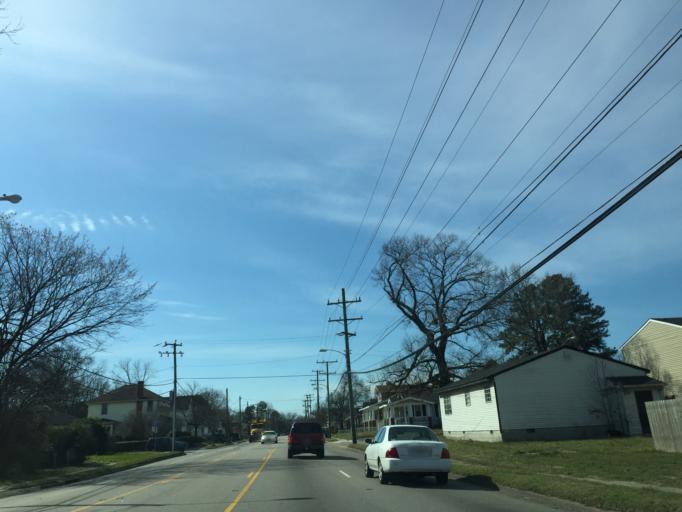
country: US
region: Virginia
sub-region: City of Norfolk
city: Norfolk
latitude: 36.8739
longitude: -76.2649
